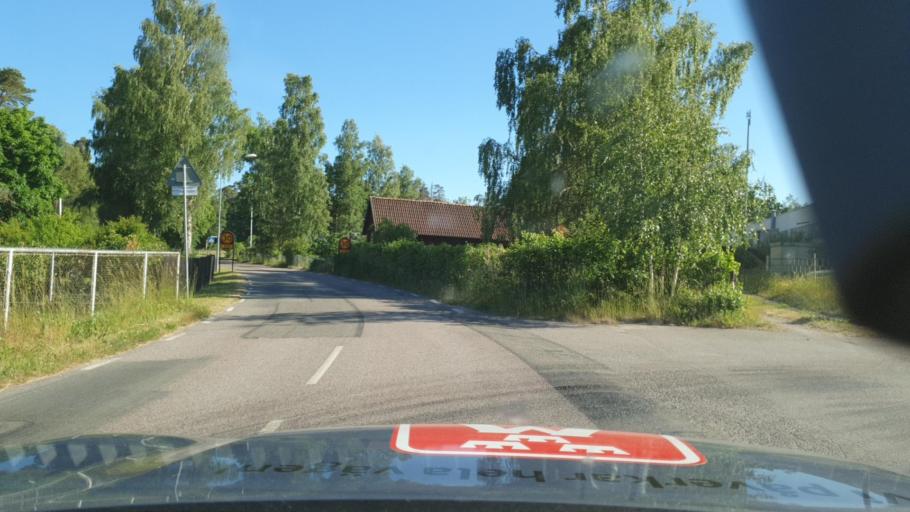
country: SE
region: Kalmar
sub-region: Torsas Kommun
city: Torsas
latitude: 56.4983
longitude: 16.1021
